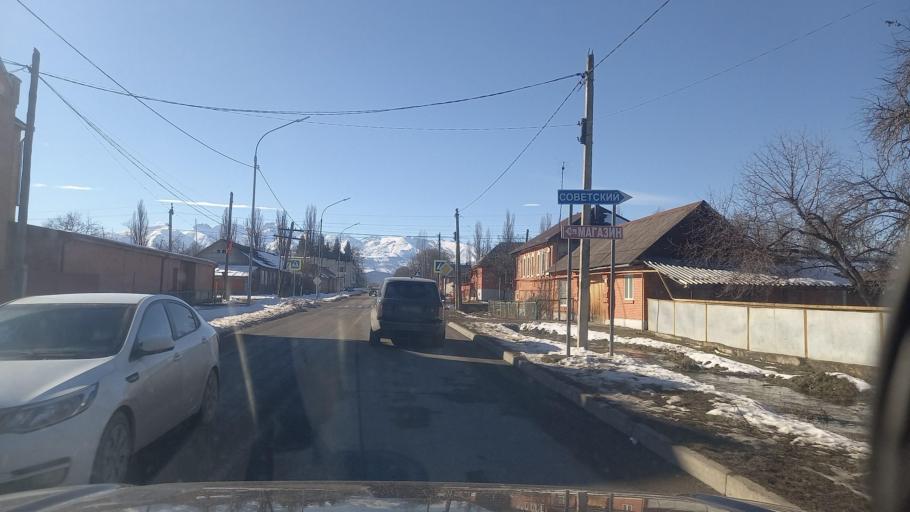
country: RU
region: North Ossetia
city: Chikola
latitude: 43.1870
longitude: 43.9019
